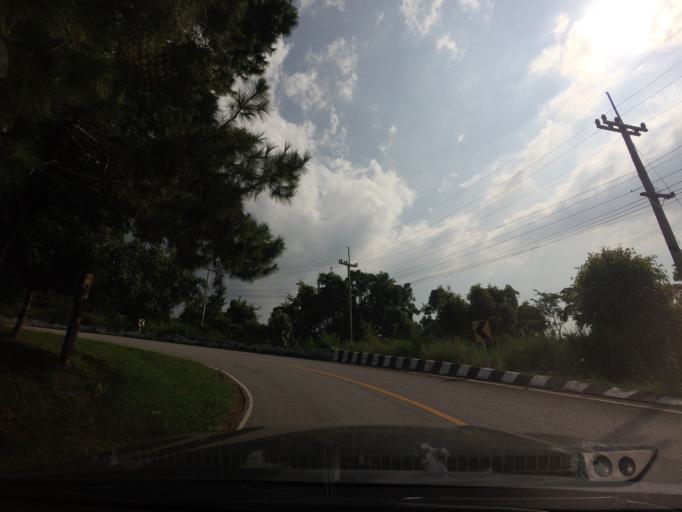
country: TH
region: Phitsanulok
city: Nakhon Thai
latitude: 17.0209
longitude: 100.9645
